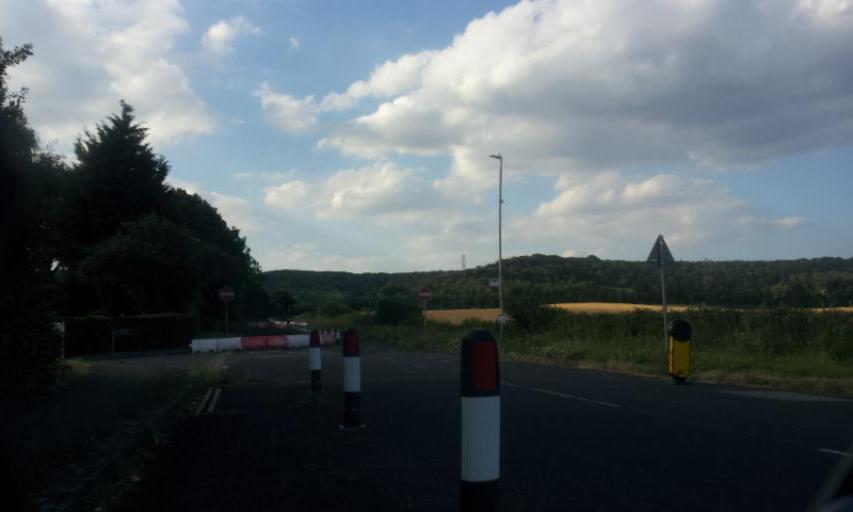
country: GB
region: England
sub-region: Kent
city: Boxley
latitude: 51.3081
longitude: 0.5143
